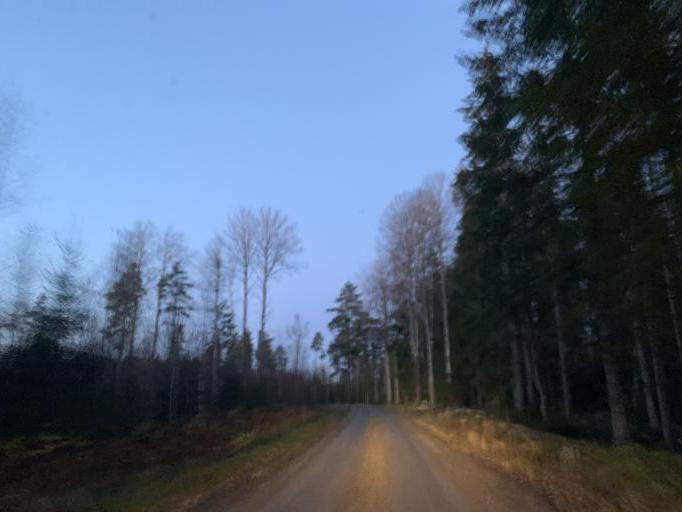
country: SE
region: OErebro
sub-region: Lindesbergs Kommun
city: Fellingsbro
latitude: 59.3703
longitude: 15.6043
